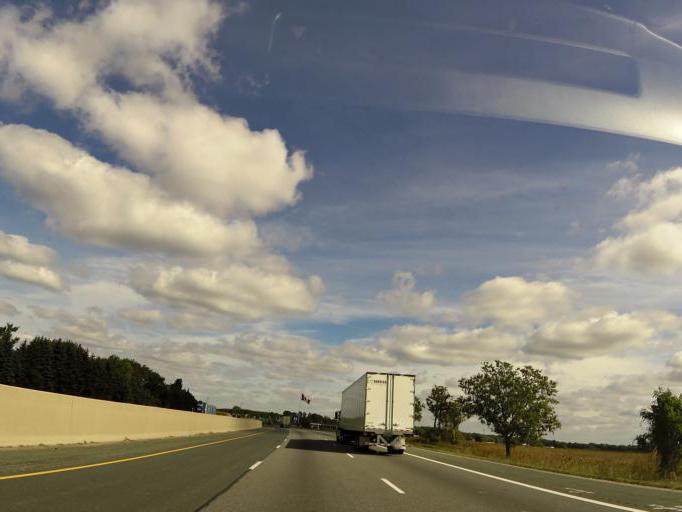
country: CA
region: Ontario
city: Dorchester
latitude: 42.9443
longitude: -81.1140
